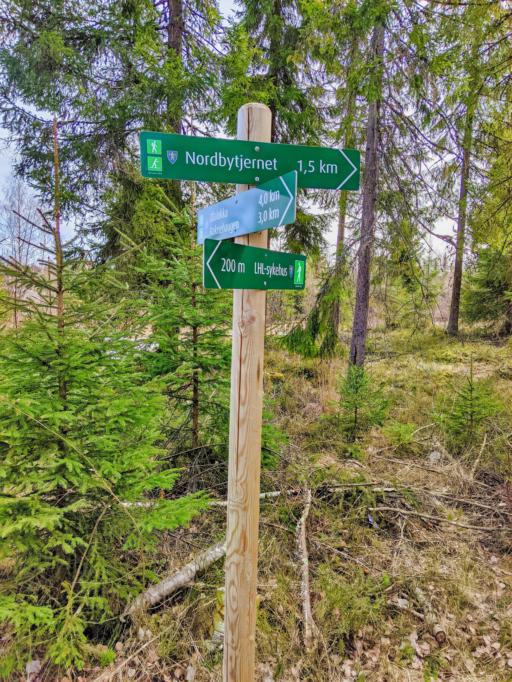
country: NO
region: Akershus
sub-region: Ullensaker
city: Jessheim
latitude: 60.1638
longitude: 11.1644
